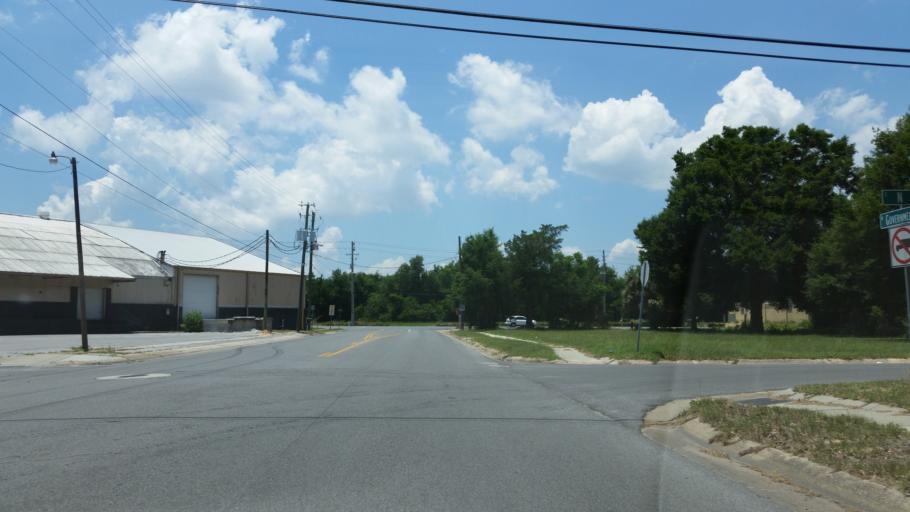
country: US
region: Florida
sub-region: Escambia County
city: Pensacola
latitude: 30.4079
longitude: -87.2407
